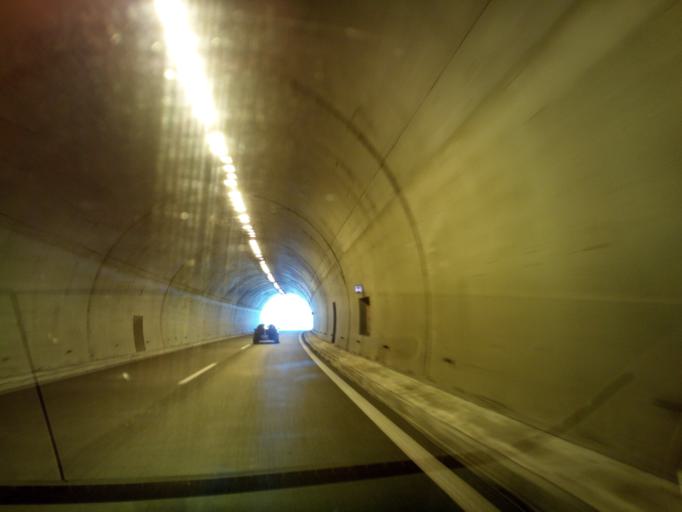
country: GR
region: Central Macedonia
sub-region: Nomos Thessalonikis
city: Nea Vrasna
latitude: 40.7011
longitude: 23.6492
